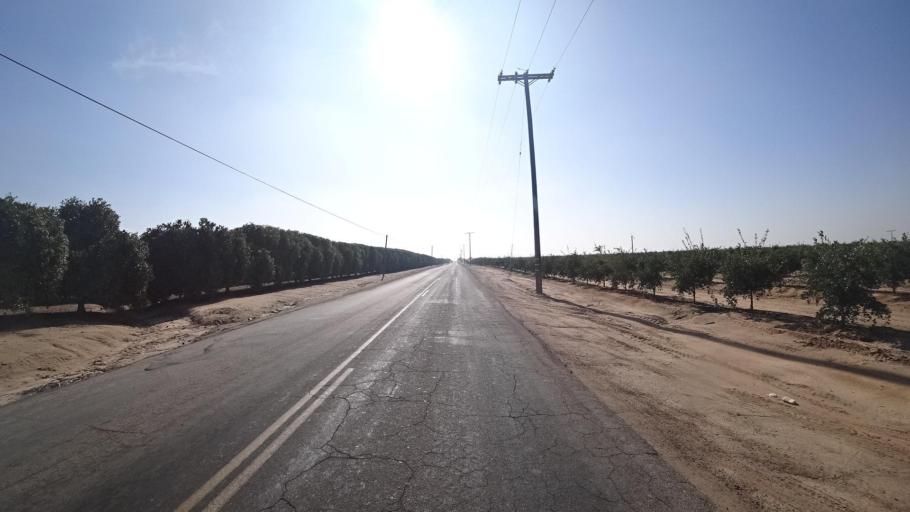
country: US
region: California
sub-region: Kern County
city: McFarland
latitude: 35.6731
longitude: -119.1340
